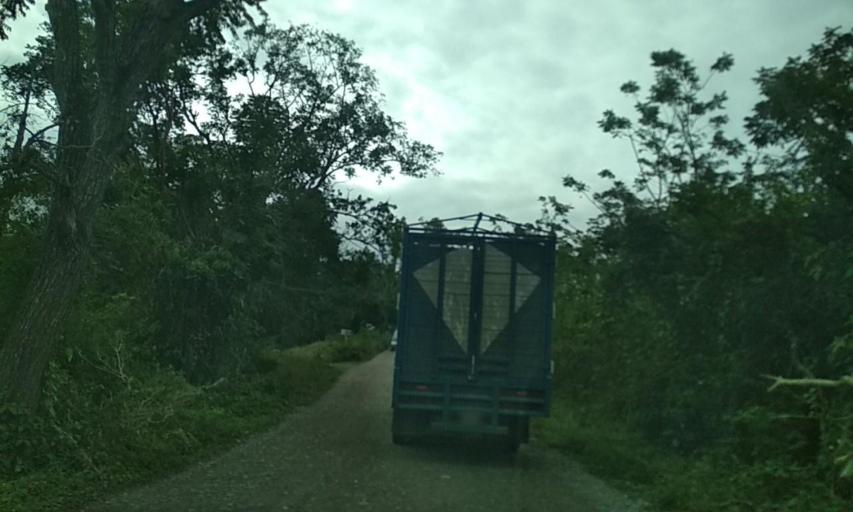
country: MX
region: Veracruz
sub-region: Papantla
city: Residencial Tajin
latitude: 20.6272
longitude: -97.3638
